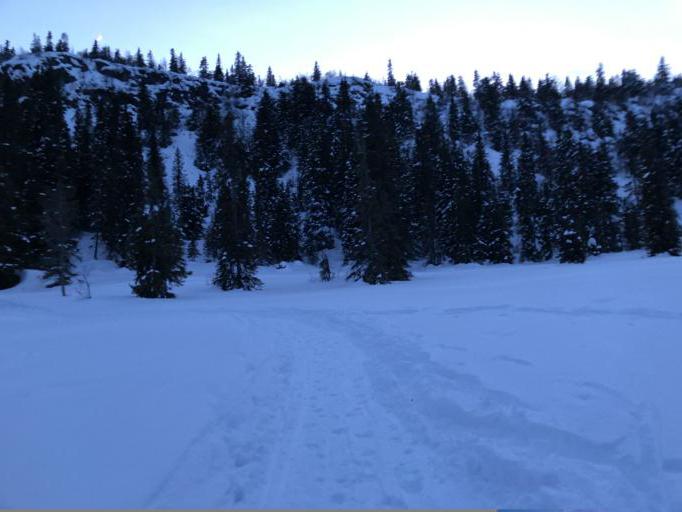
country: NO
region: Oppland
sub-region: Gausdal
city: Segalstad bru
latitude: 61.3254
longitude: 10.0537
